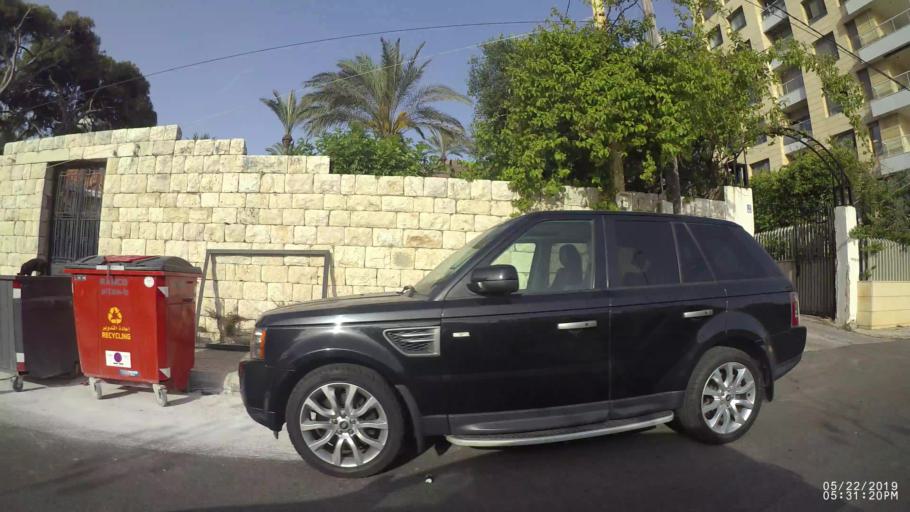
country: LB
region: Beyrouth
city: Ra's Bayrut
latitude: 33.8924
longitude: 35.4747
